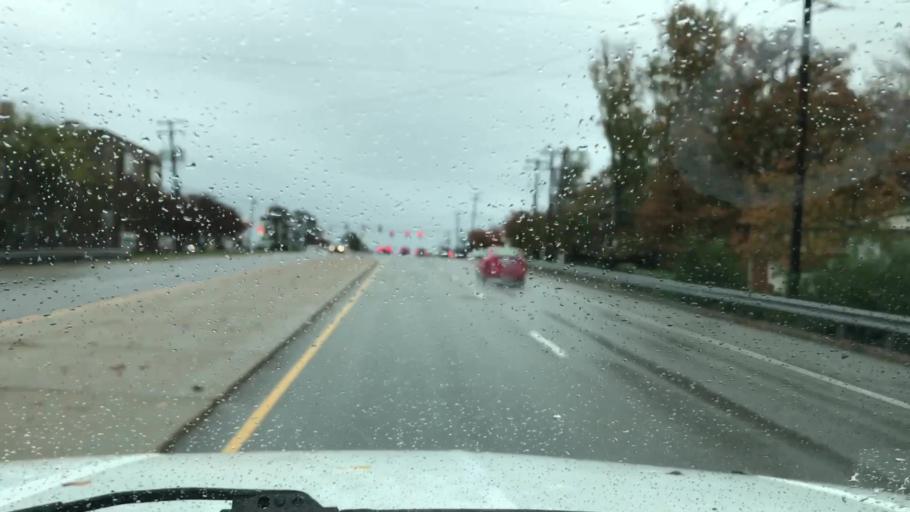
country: US
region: Virginia
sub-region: Henrico County
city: Tuckahoe
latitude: 37.5947
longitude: -77.5685
